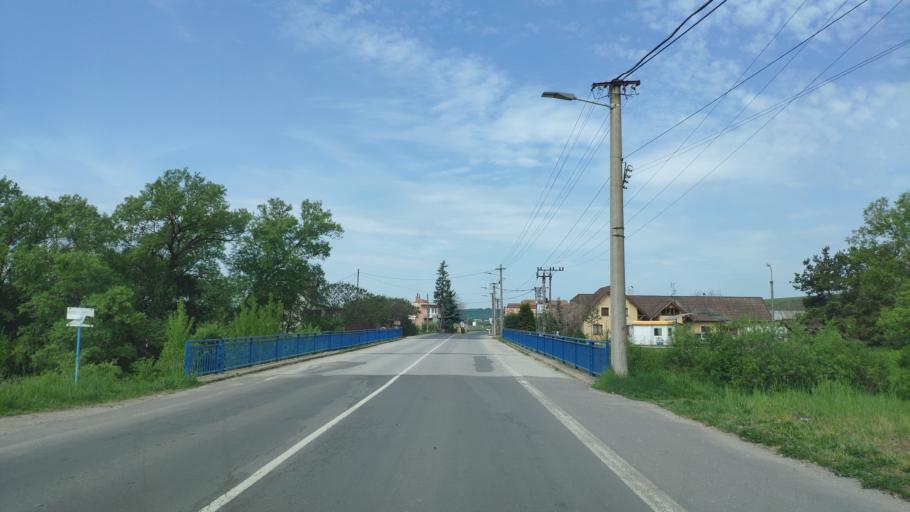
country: HU
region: Borsod-Abauj-Zemplen
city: Putnok
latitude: 48.4238
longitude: 20.3171
